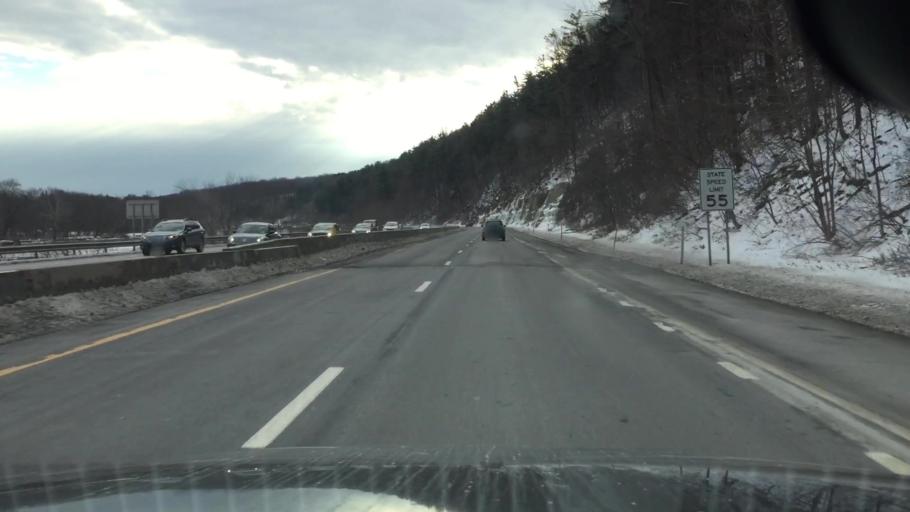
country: US
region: New York
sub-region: Broome County
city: Chenango Bridge
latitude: 42.1623
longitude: -75.8630
